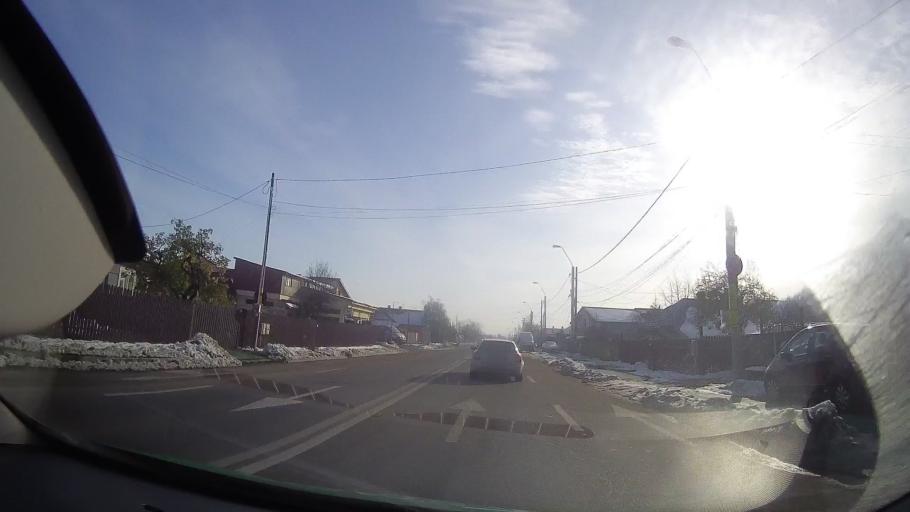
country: RO
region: Neamt
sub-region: Comuna Garcina
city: Garcina
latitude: 46.9592
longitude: 26.3824
